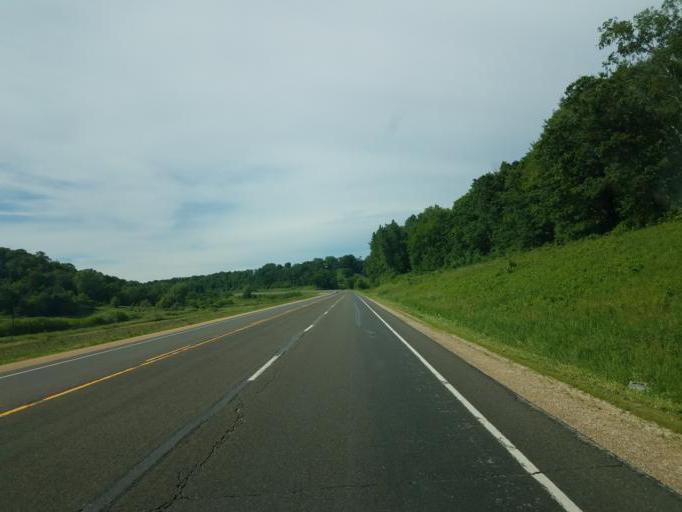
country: US
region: Wisconsin
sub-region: Monroe County
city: Tomah
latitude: 43.8821
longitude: -90.4809
